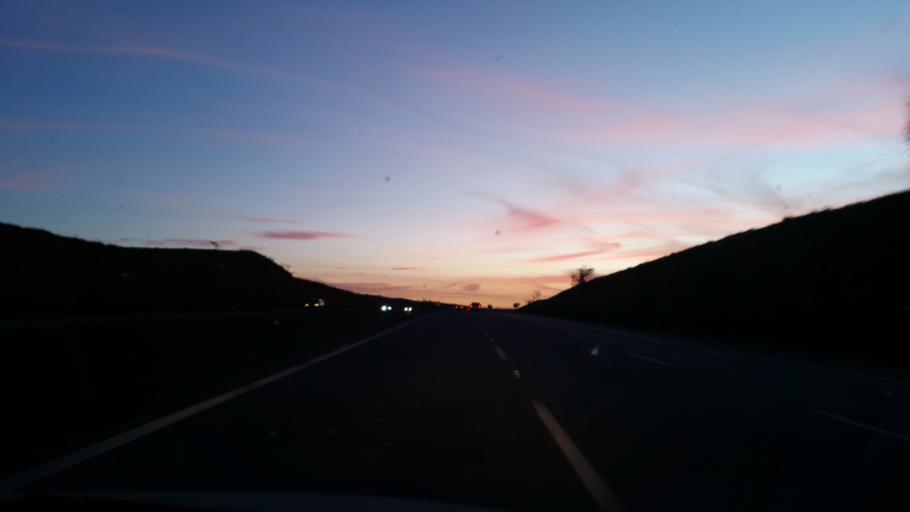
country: BR
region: Sao Paulo
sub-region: Guararema
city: Guararema
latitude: -23.3585
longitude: -46.0697
